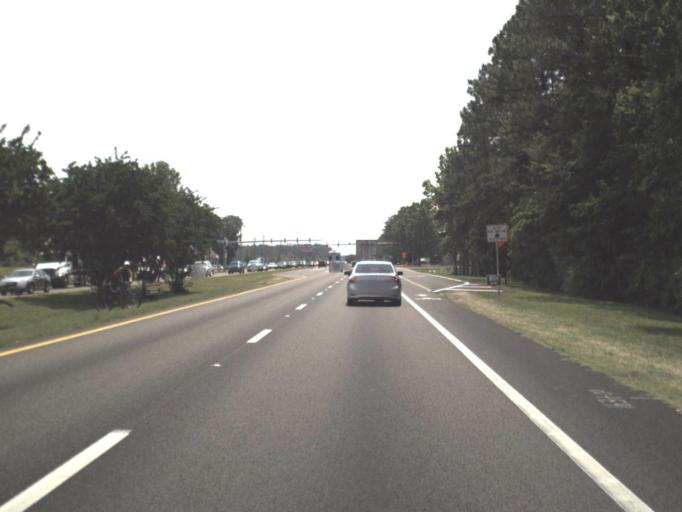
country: US
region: Florida
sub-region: Nassau County
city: Yulee
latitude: 30.6267
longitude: -81.5500
